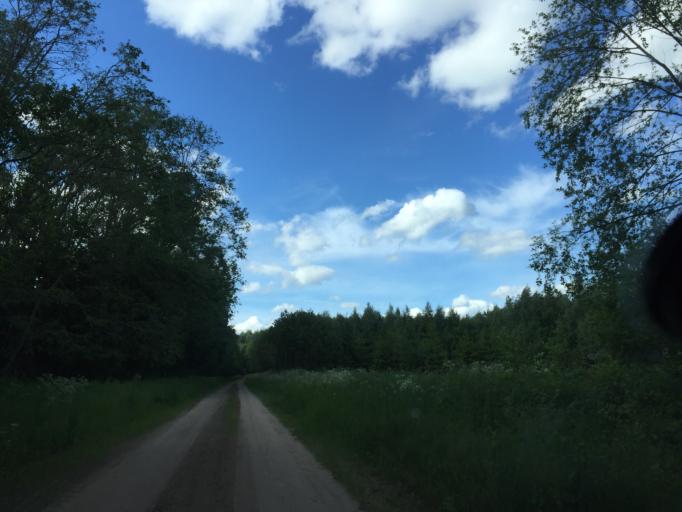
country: LV
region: Vecumnieki
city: Vecumnieki
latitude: 56.4257
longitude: 24.6134
